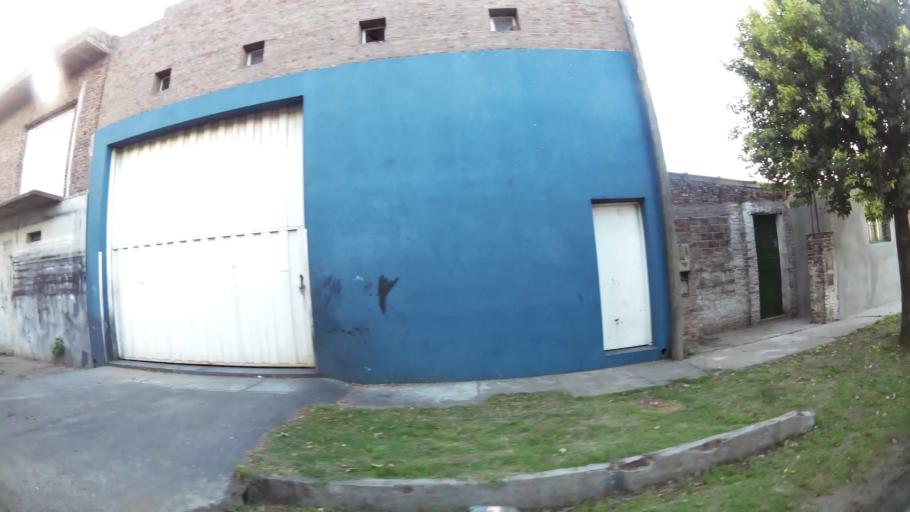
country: AR
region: Santa Fe
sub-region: Departamento de Rosario
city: Rosario
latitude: -32.9828
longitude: -60.6640
